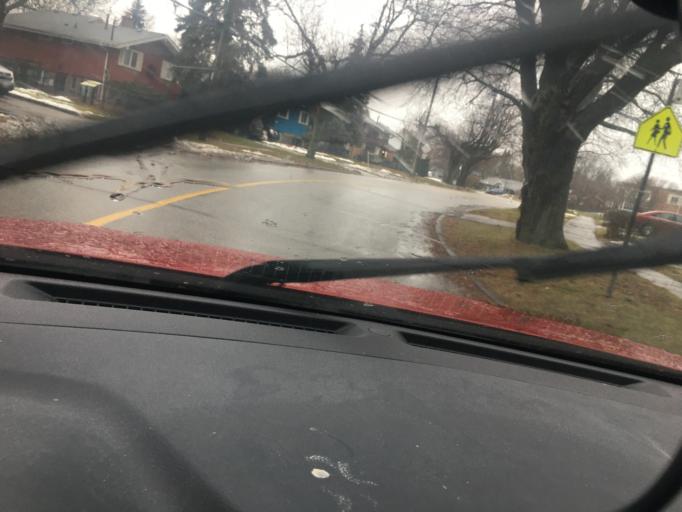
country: CA
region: Ontario
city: Scarborough
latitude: 43.7662
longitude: -79.2646
